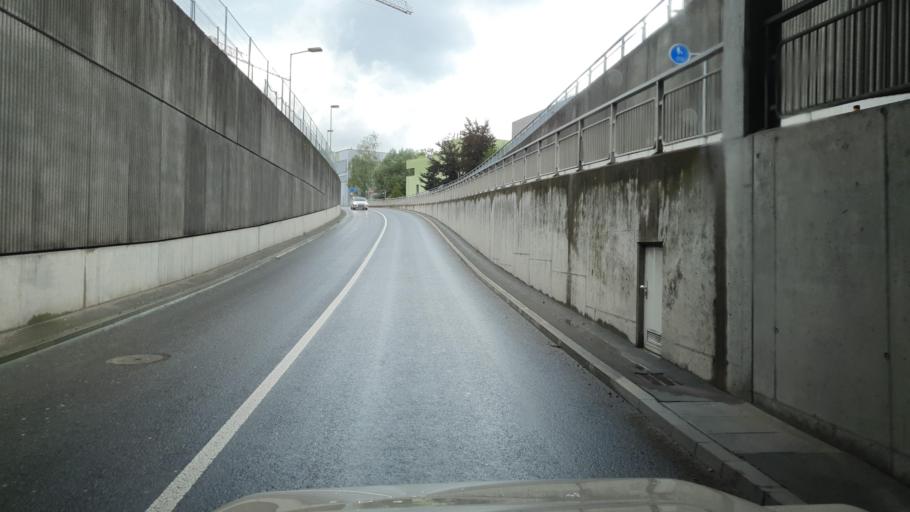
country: CH
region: Lucerne
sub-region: Lucerne-Land District
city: Horw
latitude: 47.0184
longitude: 8.3065
